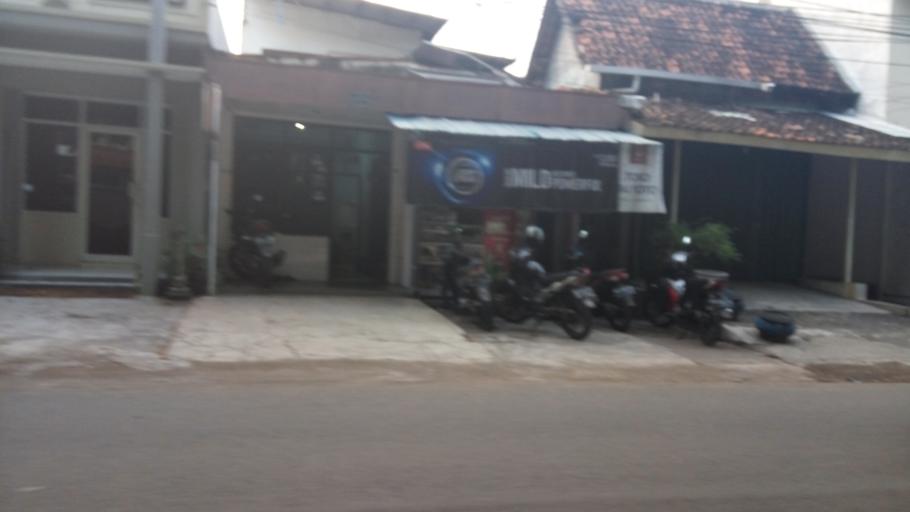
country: ID
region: Central Java
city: Semarang
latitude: -6.9866
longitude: 110.4073
